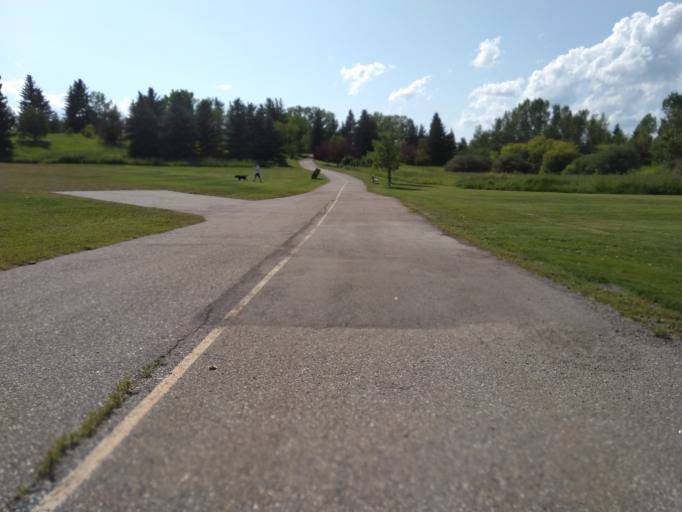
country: CA
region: Alberta
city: Calgary
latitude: 51.0790
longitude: -114.1066
